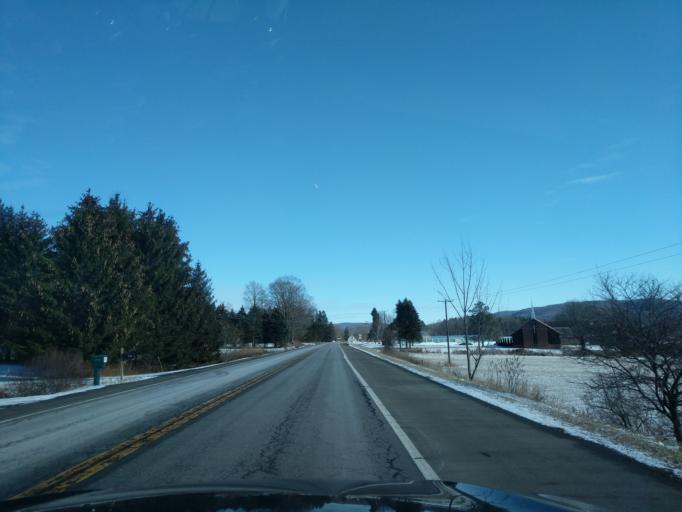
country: US
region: New York
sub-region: Tompkins County
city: East Ithaca
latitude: 42.3955
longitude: -76.3853
